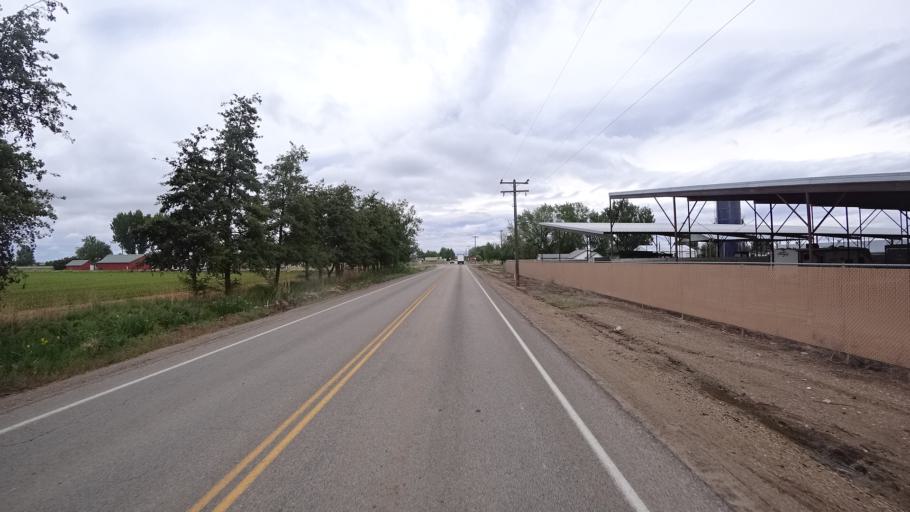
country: US
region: Idaho
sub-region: Ada County
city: Star
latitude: 43.6355
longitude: -116.4937
